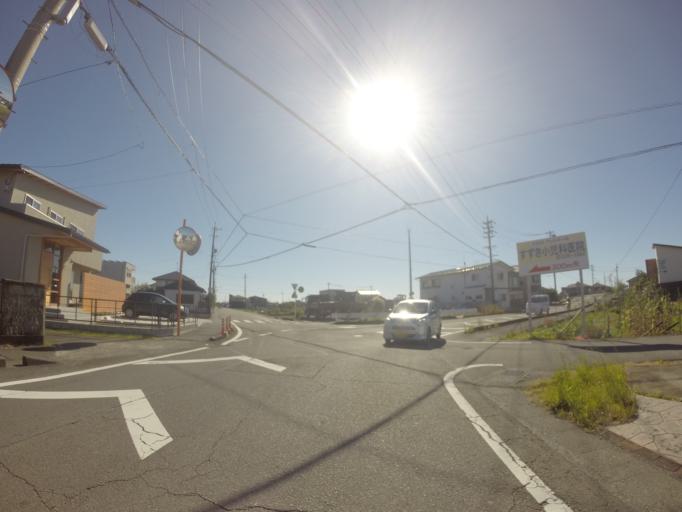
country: JP
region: Shizuoka
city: Fujieda
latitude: 34.8401
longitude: 138.2399
